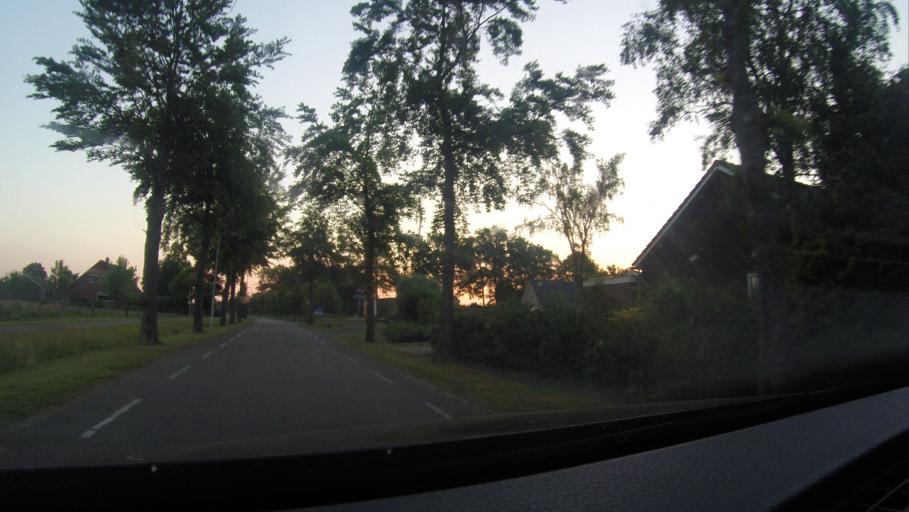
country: NL
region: Gelderland
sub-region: Gemeente Lochem
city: Harfsen
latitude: 52.2788
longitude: 6.2724
